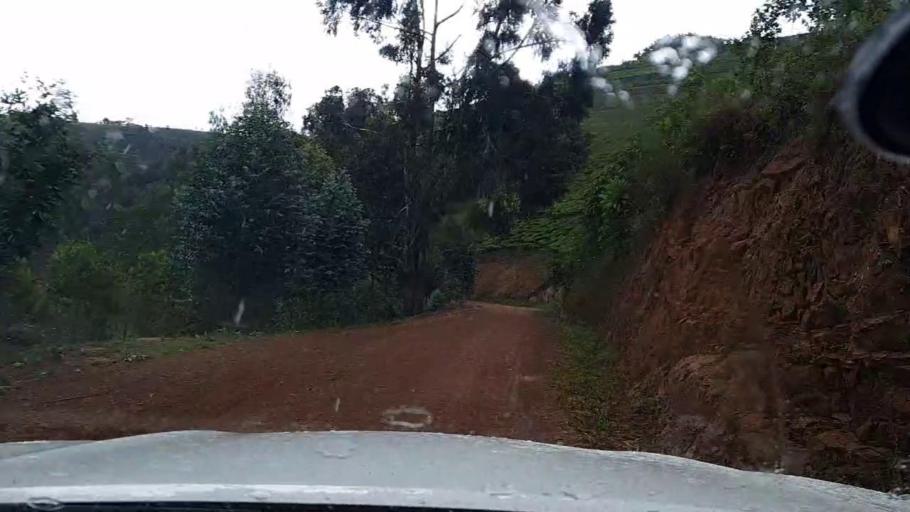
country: RW
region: Western Province
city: Kibuye
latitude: -2.1588
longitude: 29.4346
